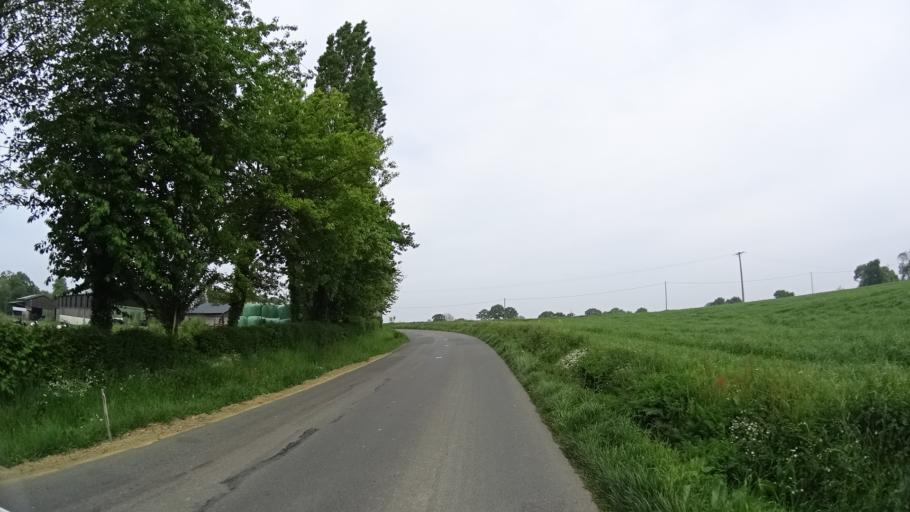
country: FR
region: Brittany
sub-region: Departement d'Ille-et-Vilaine
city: Montreuil-le-Gast
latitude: 48.2495
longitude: -1.7454
